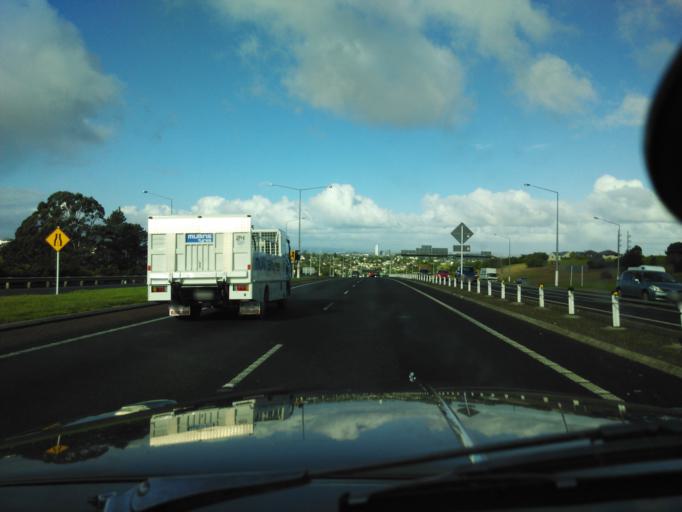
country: NZ
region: Auckland
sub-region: Auckland
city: Rothesay Bay
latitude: -36.7545
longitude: 174.7299
